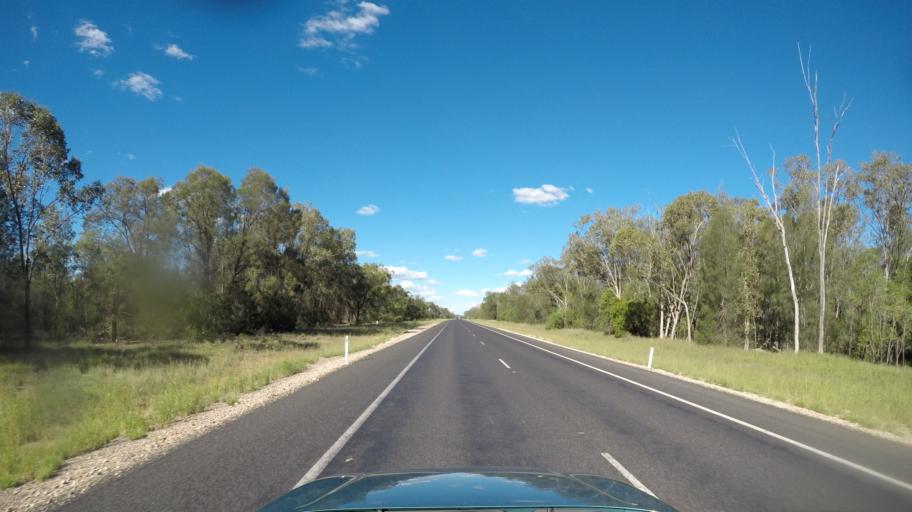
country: AU
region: Queensland
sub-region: Goondiwindi
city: Goondiwindi
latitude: -28.0574
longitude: 150.7706
